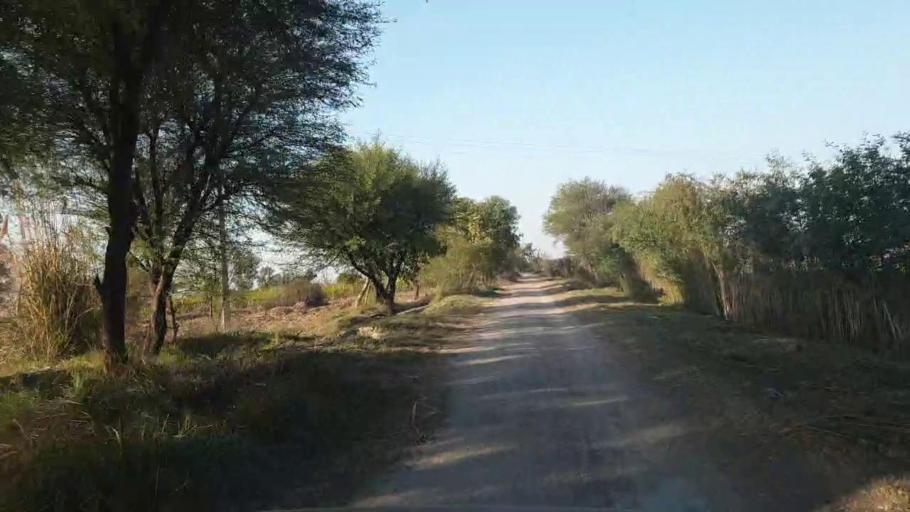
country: PK
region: Sindh
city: Tando Allahyar
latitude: 25.3744
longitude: 68.7014
